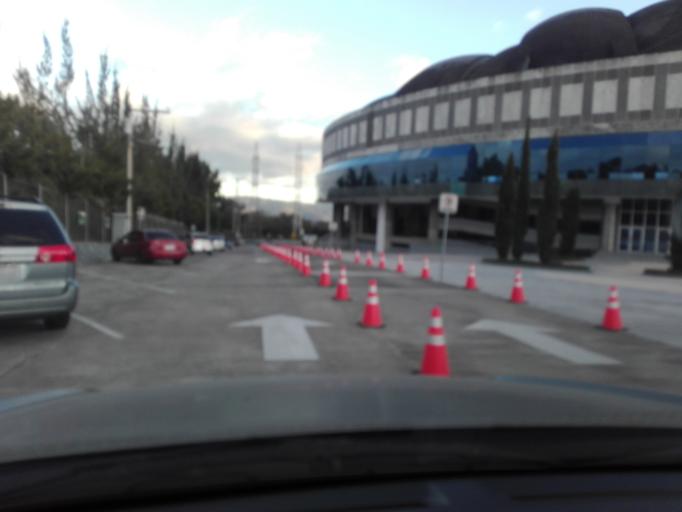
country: GT
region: Guatemala
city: Mixco
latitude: 14.5938
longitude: -90.5766
